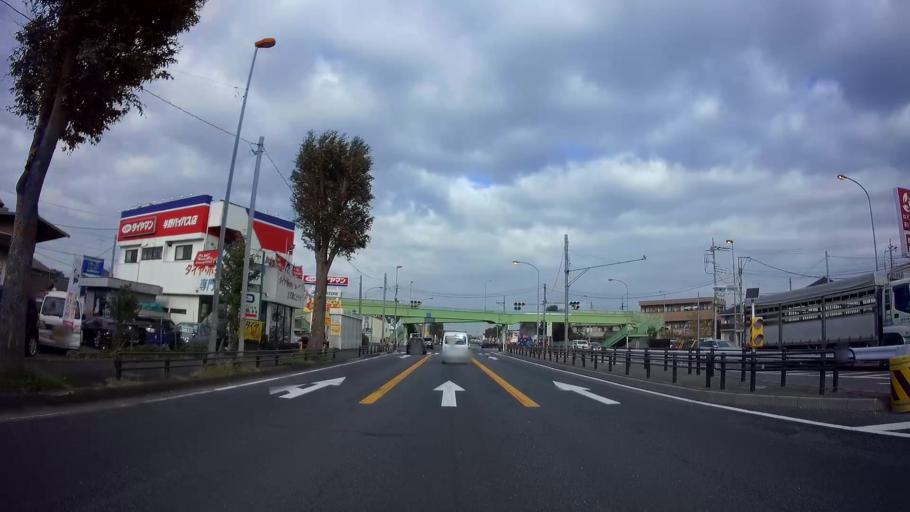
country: JP
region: Saitama
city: Yono
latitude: 35.8943
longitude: 139.6077
